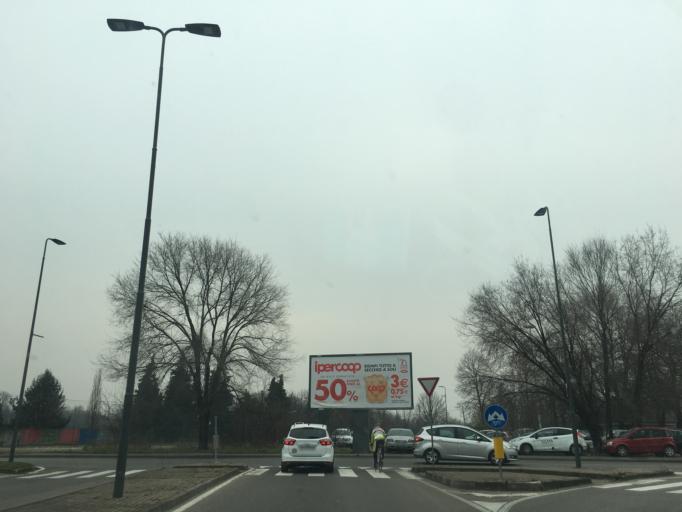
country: IT
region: Lombardy
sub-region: Citta metropolitana di Milano
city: Figino
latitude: 45.4762
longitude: 9.0938
